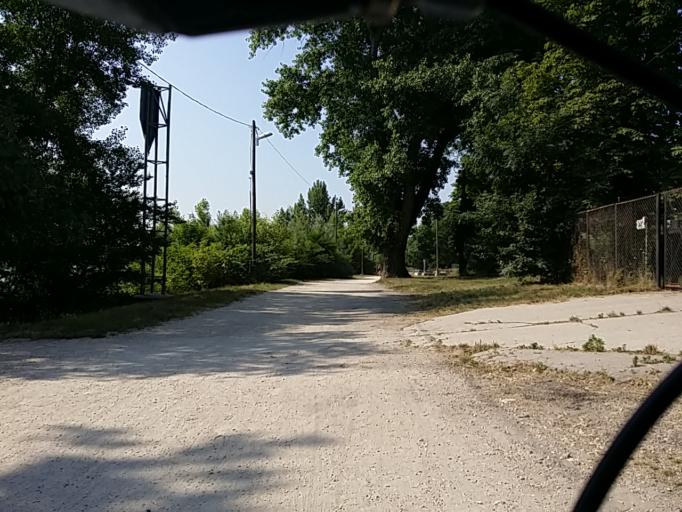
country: HU
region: Budapest
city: Budapest IV. keruelet
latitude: 47.5680
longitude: 19.0645
